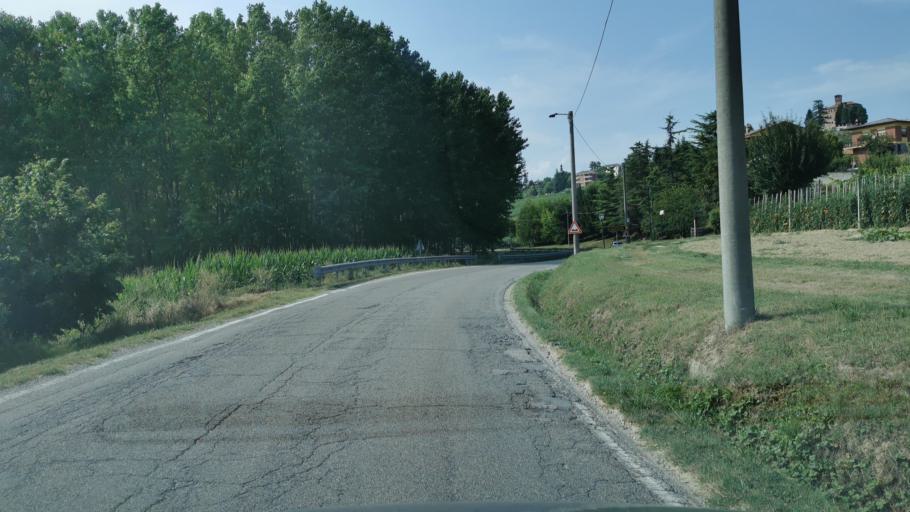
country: IT
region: Piedmont
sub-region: Provincia di Cuneo
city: Grinzane Cavour
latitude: 44.6478
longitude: 7.9953
